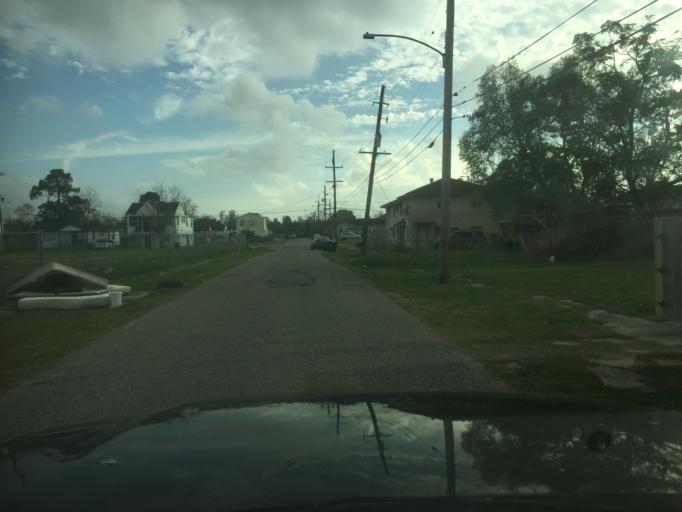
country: US
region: Louisiana
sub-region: Orleans Parish
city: New Orleans
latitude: 29.9954
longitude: -90.0806
